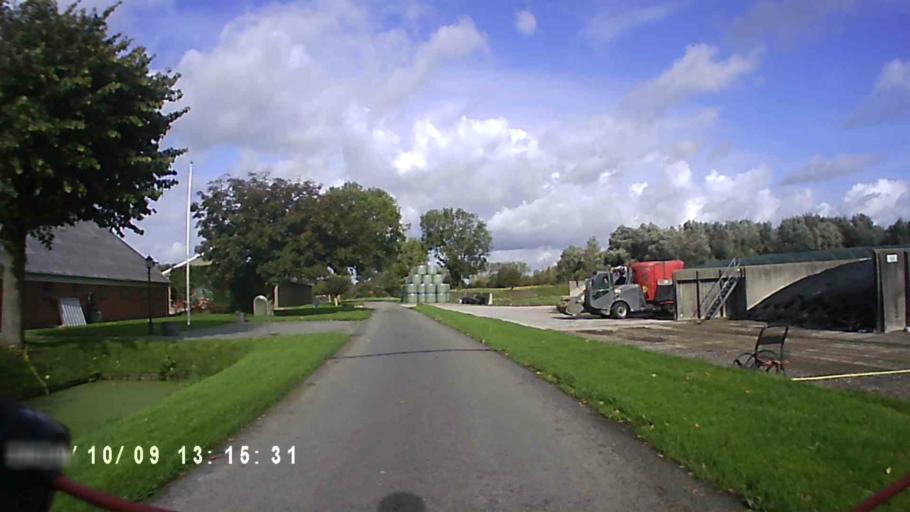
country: NL
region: Groningen
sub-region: Gemeente Zuidhorn
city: Aduard
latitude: 53.2555
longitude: 6.4336
